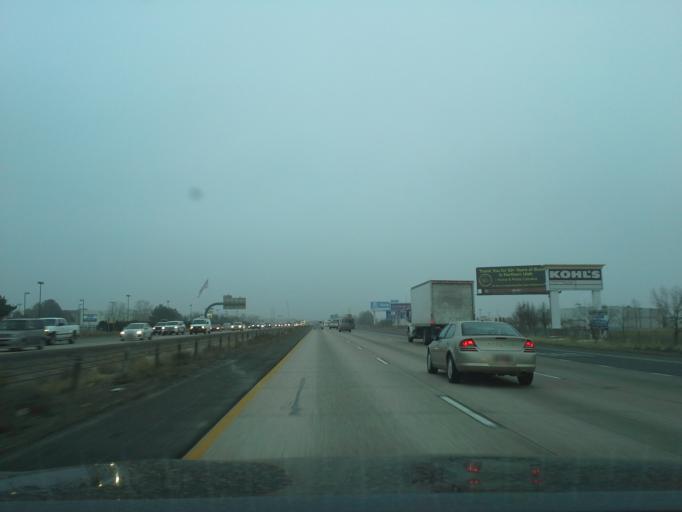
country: US
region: Utah
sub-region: Davis County
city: Layton
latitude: 41.0813
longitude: -111.9836
